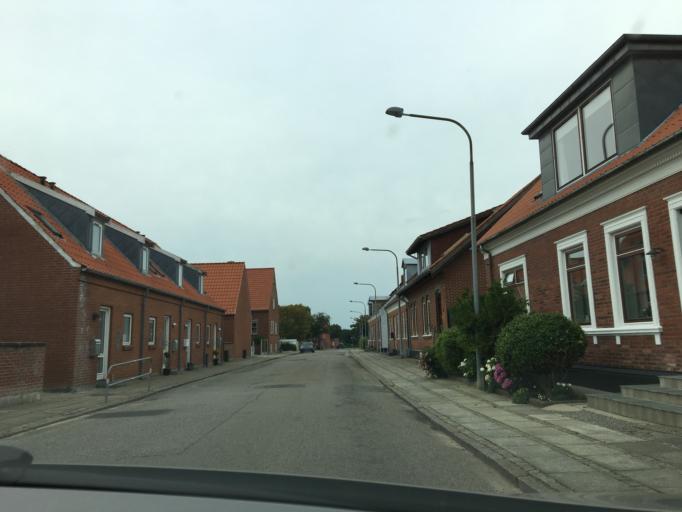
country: DK
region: Central Jutland
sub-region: Ringkobing-Skjern Kommune
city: Ringkobing
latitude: 56.0900
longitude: 8.2480
